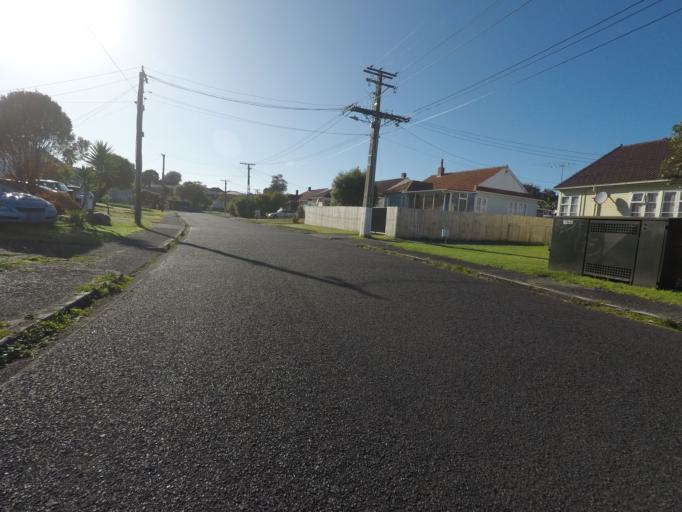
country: NZ
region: Auckland
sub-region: Auckland
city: Rosebank
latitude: -36.8982
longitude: 174.7153
